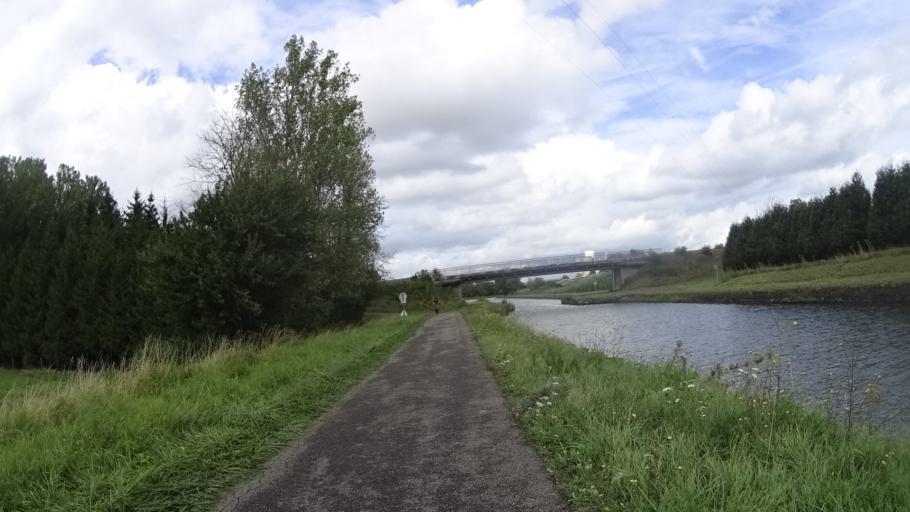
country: FR
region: Lorraine
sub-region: Departement de la Moselle
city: Lorquin
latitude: 48.6845
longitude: 6.9526
